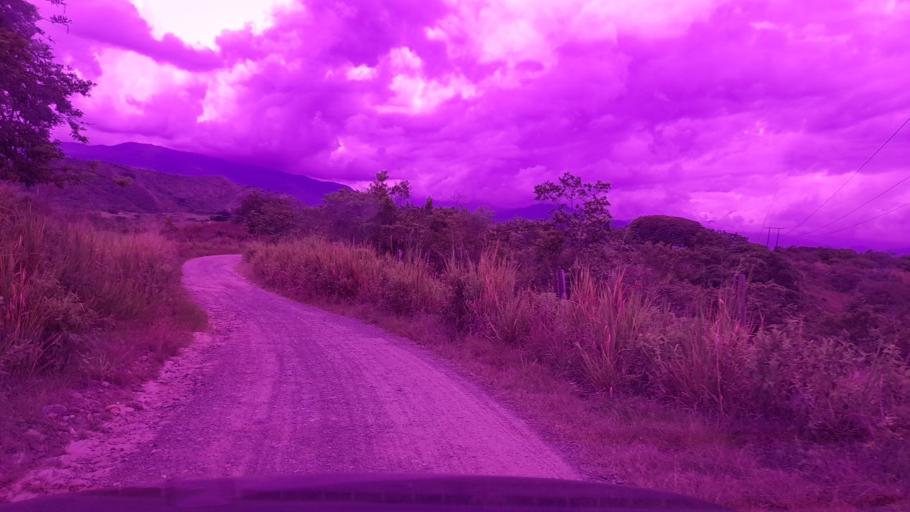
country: CO
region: Valle del Cauca
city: Bugalagrande
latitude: 4.1857
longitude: -76.1373
